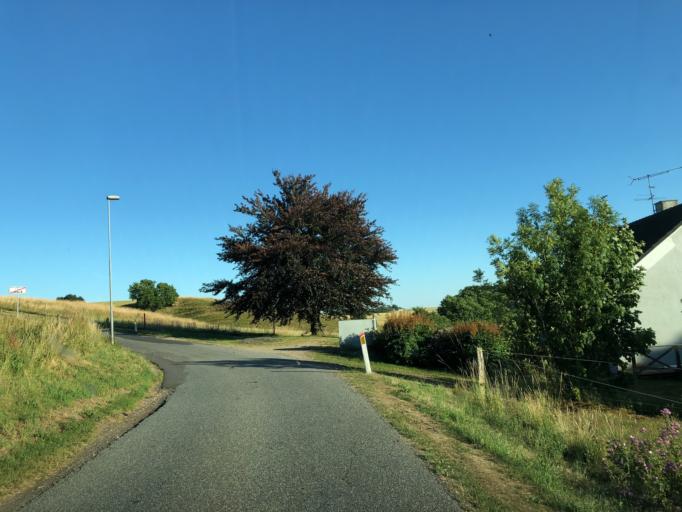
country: DK
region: Central Jutland
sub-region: Skanderborg Kommune
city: Ry
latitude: 55.9863
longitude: 9.7897
